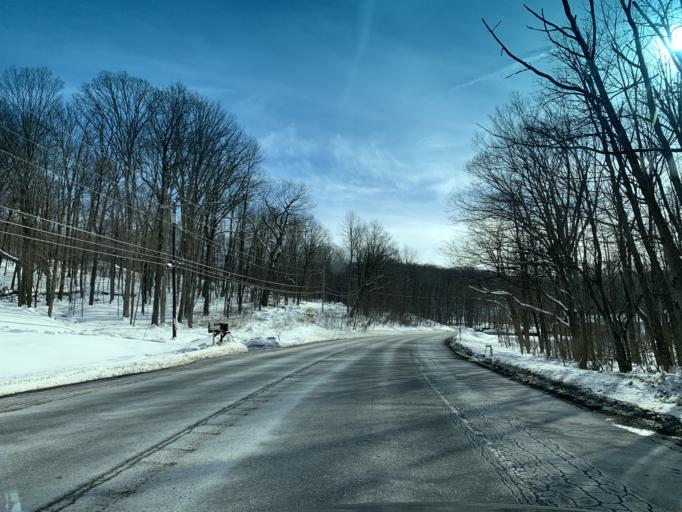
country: US
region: Maryland
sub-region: Allegany County
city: Frostburg
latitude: 39.6225
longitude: -78.8998
